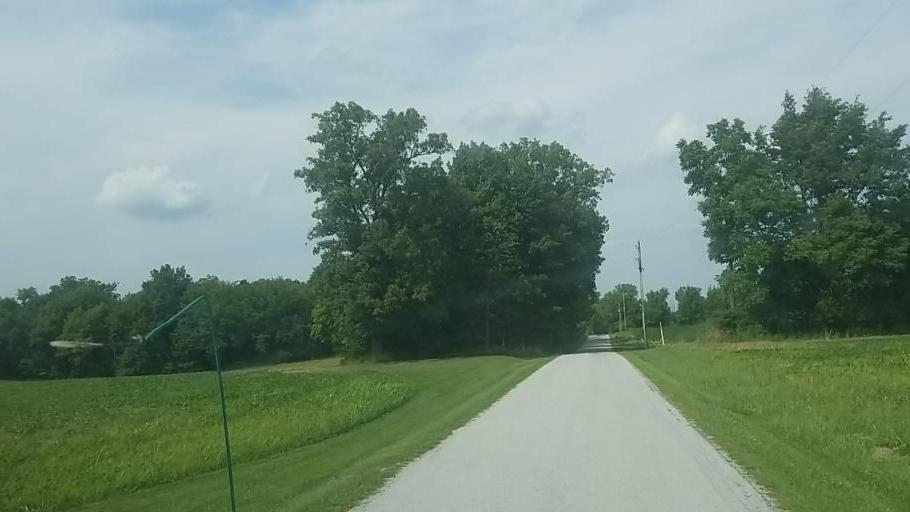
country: US
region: Ohio
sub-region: Hardin County
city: Forest
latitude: 40.7924
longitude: -83.5524
